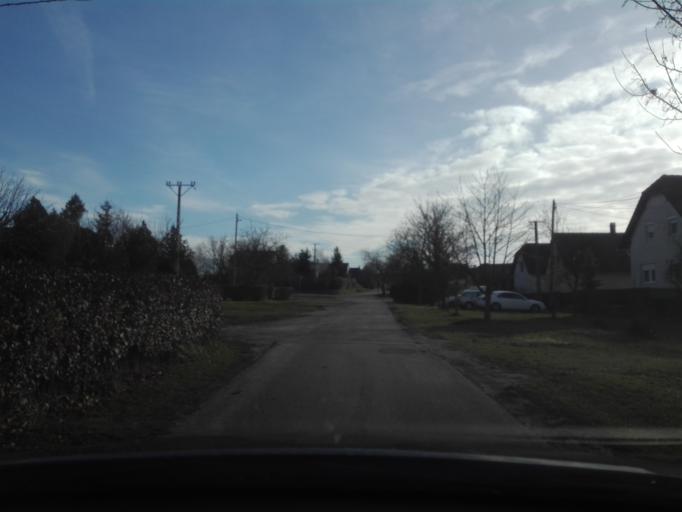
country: HU
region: Veszprem
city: Balatonfured
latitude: 47.0081
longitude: 17.7820
